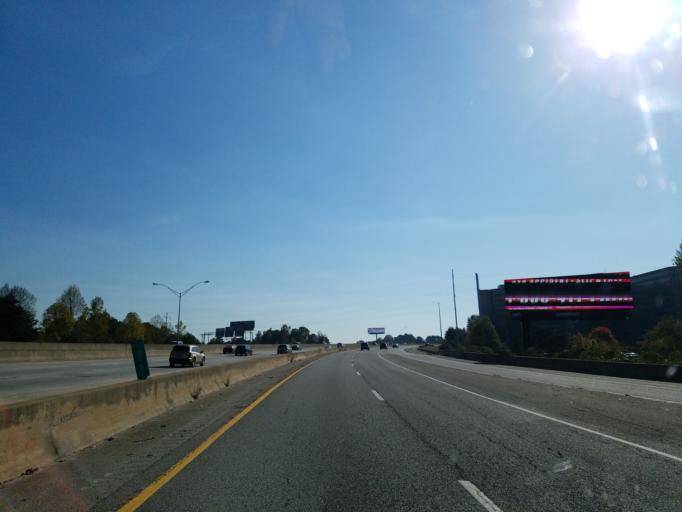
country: US
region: Georgia
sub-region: Fulton County
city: College Park
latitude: 33.6291
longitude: -84.4561
